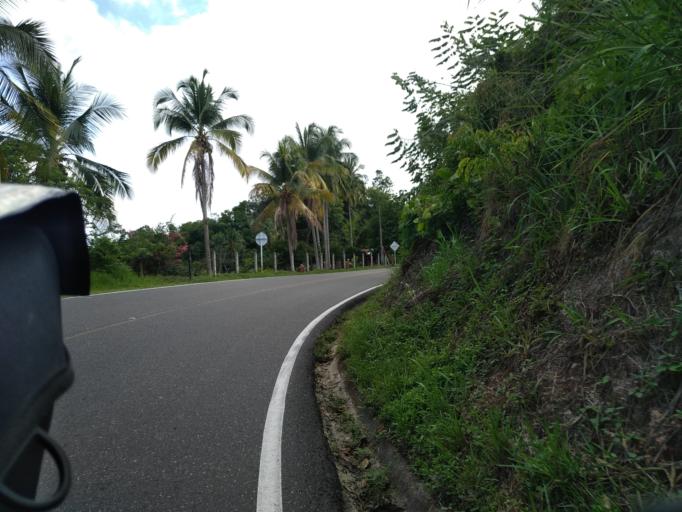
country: CO
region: Santander
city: Cimitarra
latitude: 6.4250
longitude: -74.0113
